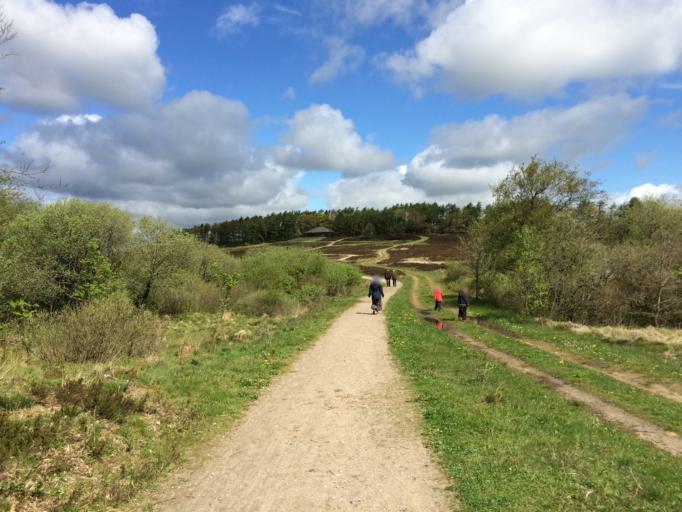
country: DK
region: Central Jutland
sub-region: Holstebro Kommune
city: Holstebro
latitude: 56.2276
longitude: 8.6210
